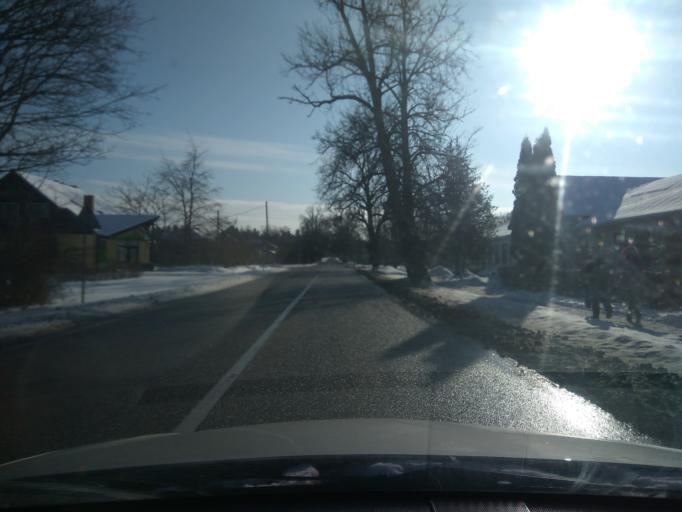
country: LV
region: Kuldigas Rajons
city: Kuldiga
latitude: 57.2797
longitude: 22.0224
